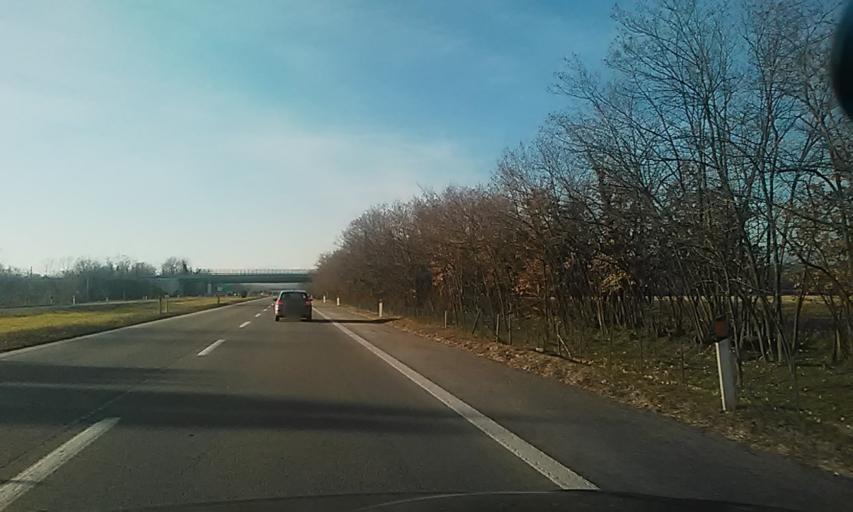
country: IT
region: Piedmont
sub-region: Provincia di Vercelli
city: Alice Castello
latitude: 45.3772
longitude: 8.0844
